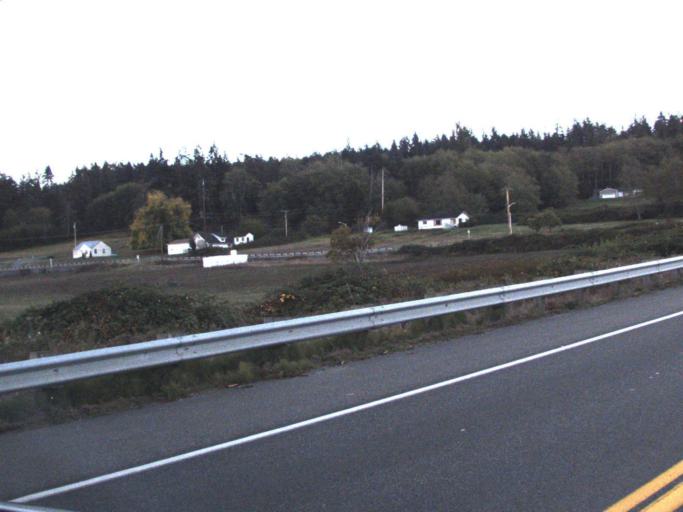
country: US
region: Washington
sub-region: Island County
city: Ault Field
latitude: 48.3500
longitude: -122.6124
